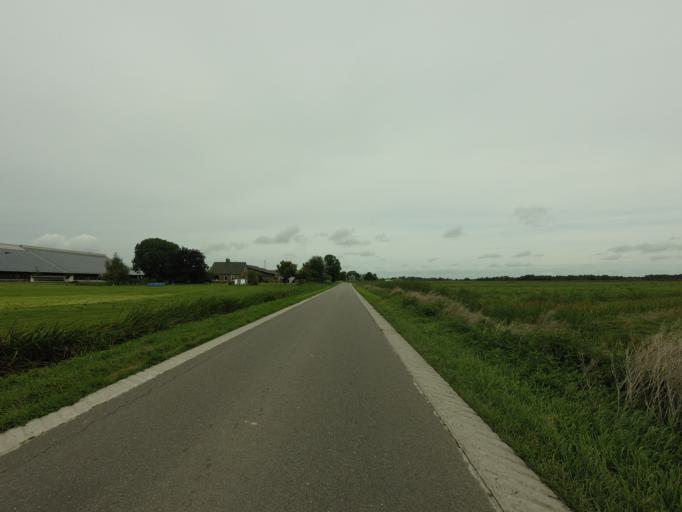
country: NL
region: Overijssel
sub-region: Gemeente Steenwijkerland
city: Blokzijl
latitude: 52.7411
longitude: 5.9666
